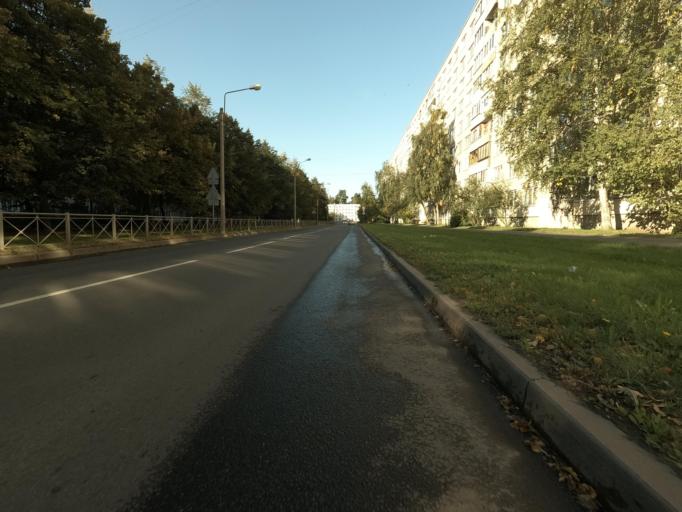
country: RU
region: St.-Petersburg
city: Kolpino
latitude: 59.7398
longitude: 30.5691
